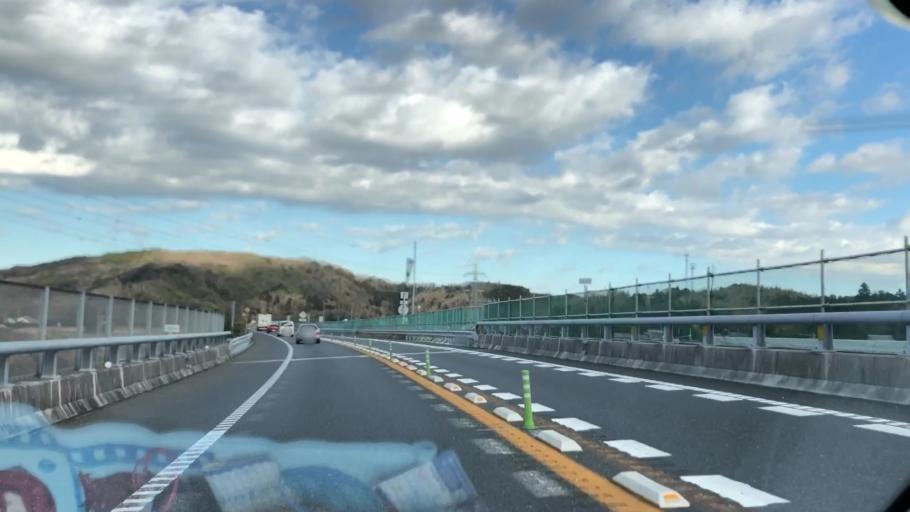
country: JP
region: Chiba
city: Kimitsu
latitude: 35.2188
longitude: 139.8856
